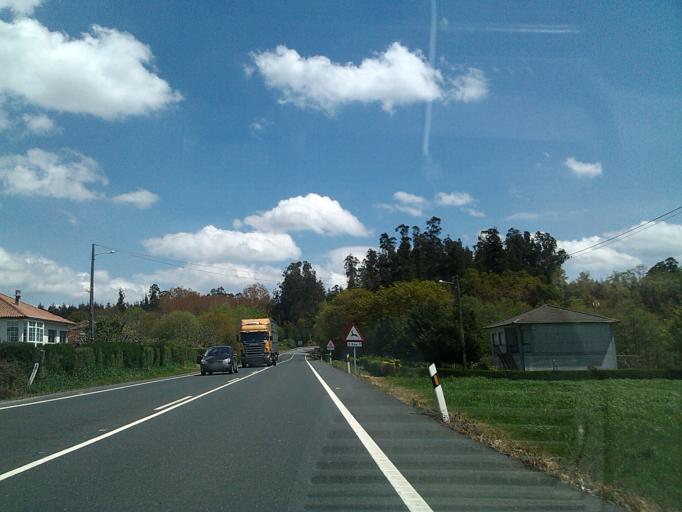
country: ES
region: Galicia
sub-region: Provincia da Coruna
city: Santiso
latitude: 42.9201
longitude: -8.0646
